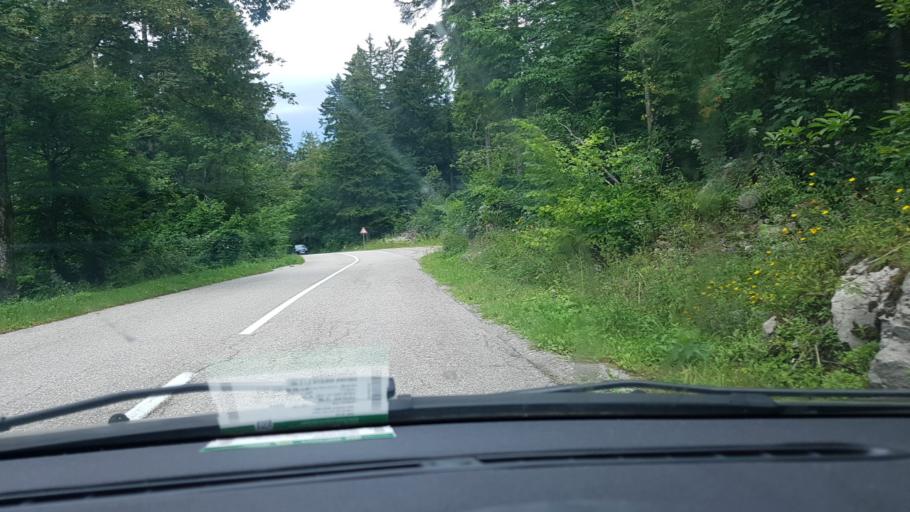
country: HR
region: Primorsko-Goranska
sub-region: Grad Delnice
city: Delnice
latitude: 45.3430
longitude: 14.7552
